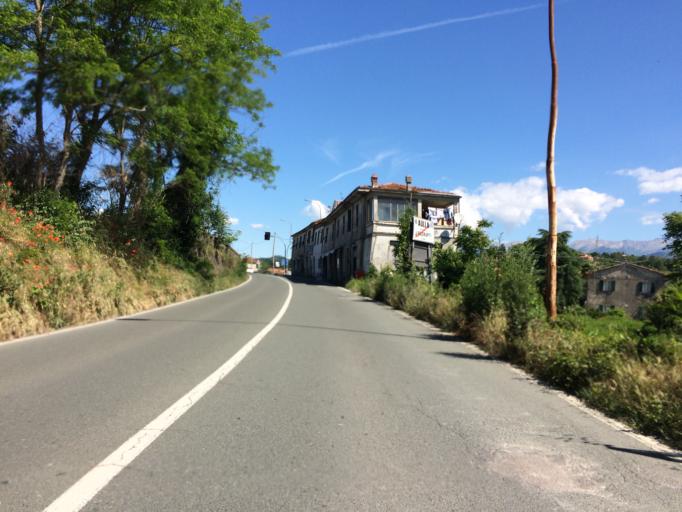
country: IT
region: Tuscany
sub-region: Provincia di Massa-Carrara
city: Terrarossa
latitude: 44.2223
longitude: 9.9701
